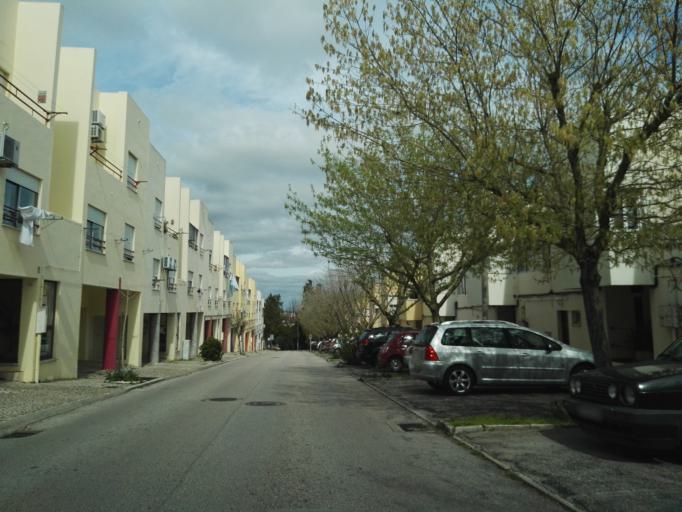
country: PT
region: Lisbon
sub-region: Vila Franca de Xira
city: Sobralinho
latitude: 38.8950
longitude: -9.0434
